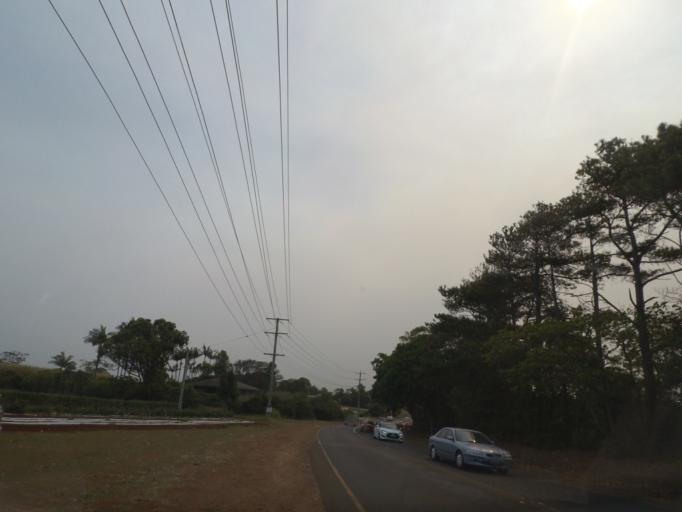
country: AU
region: New South Wales
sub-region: Tweed
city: Kingscliff
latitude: -28.2663
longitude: 153.5658
